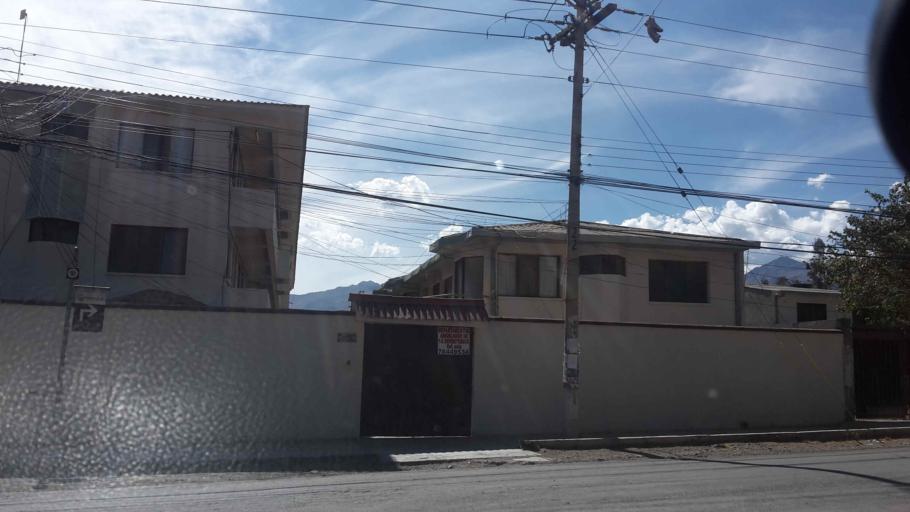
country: BO
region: Cochabamba
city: Cochabamba
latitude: -17.3359
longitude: -66.2261
